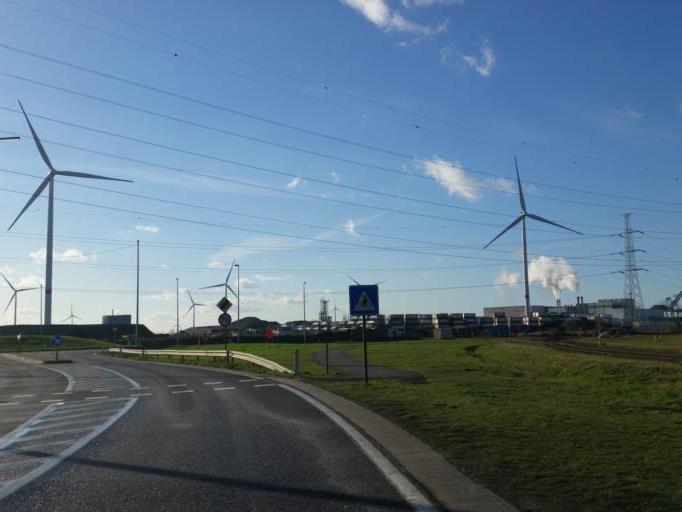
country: BE
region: Flanders
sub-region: Provincie Antwerpen
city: Zwijndrecht
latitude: 51.2872
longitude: 4.2873
